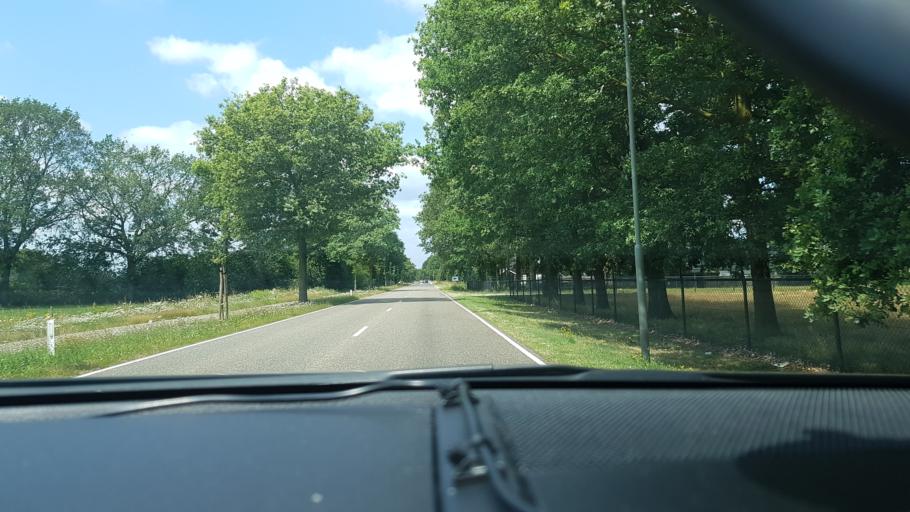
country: NL
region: Limburg
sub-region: Gemeente Leudal
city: Kelpen-Oler
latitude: 51.2473
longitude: 5.8130
